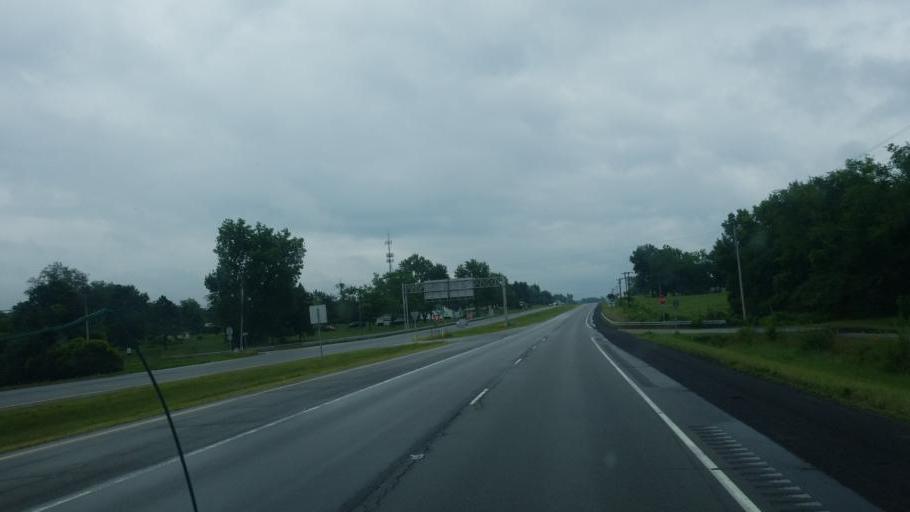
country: US
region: Indiana
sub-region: Allen County
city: New Haven
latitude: 40.9764
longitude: -85.0821
